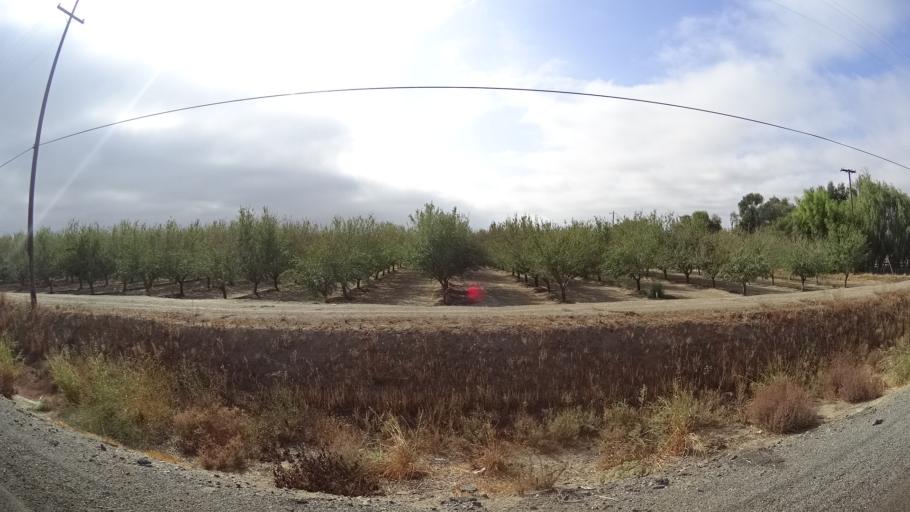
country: US
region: California
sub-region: Yolo County
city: Dunnigan
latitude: 38.7943
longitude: -121.8852
